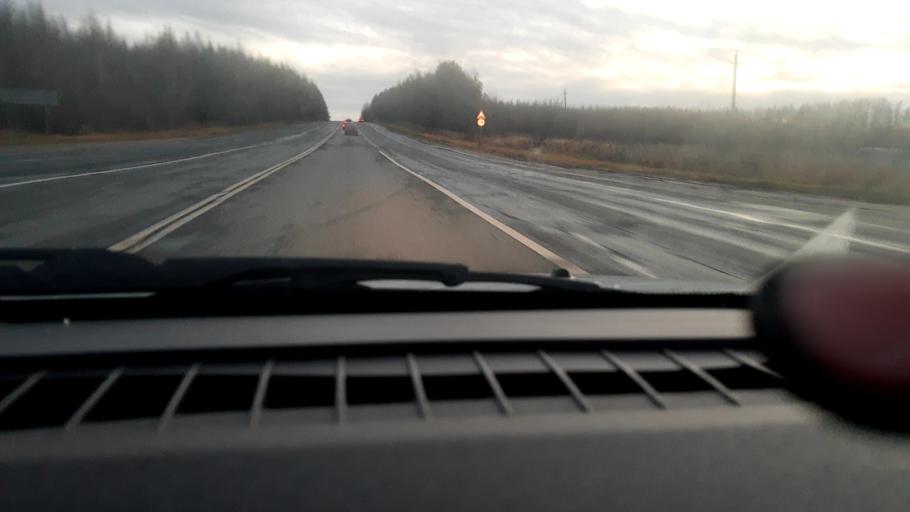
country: RU
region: Nizjnij Novgorod
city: Vladimirskoye
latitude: 56.9716
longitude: 45.1118
